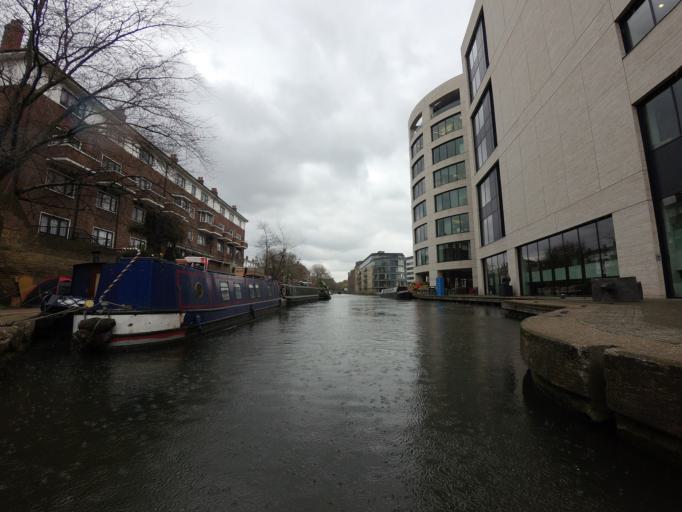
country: GB
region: England
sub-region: Greater London
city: Barnsbury
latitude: 51.5354
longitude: -0.1221
